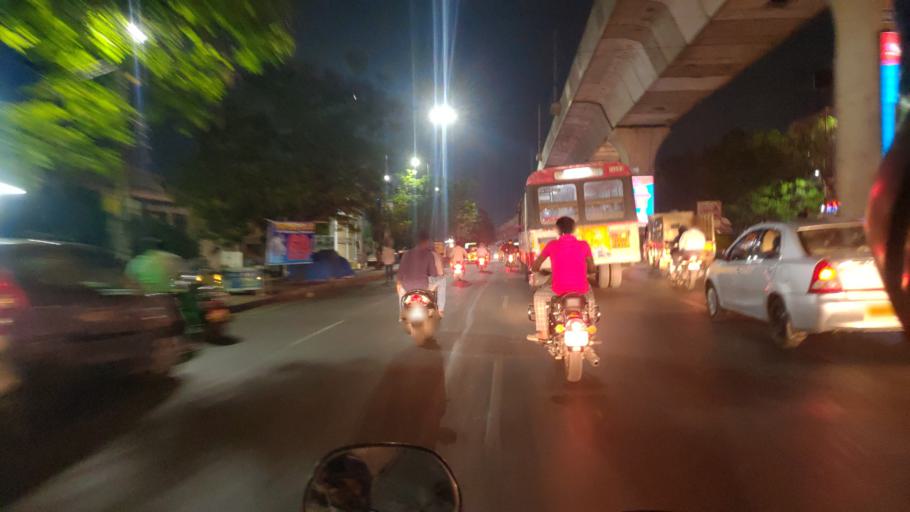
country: IN
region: Telangana
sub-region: Rangareddi
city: Gaddi Annaram
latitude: 17.3693
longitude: 78.5181
